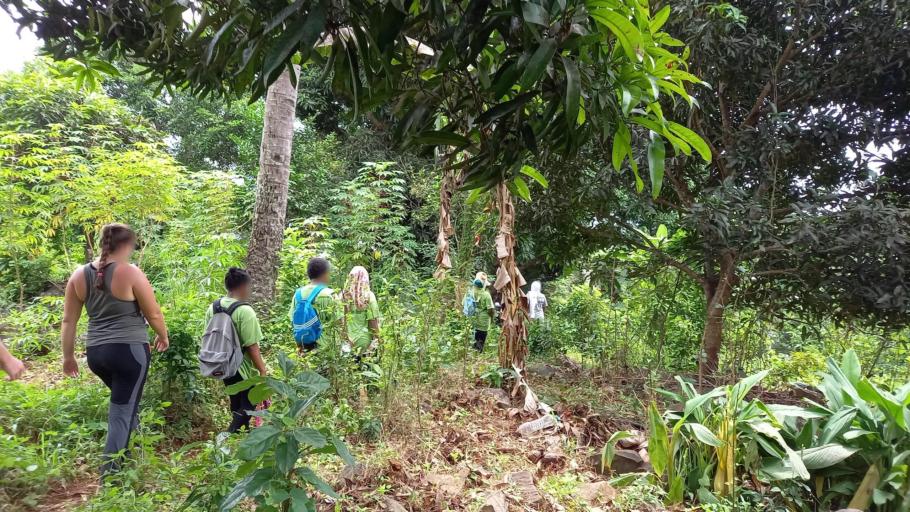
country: YT
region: Acoua
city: Acoua
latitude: -12.7117
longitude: 45.0571
